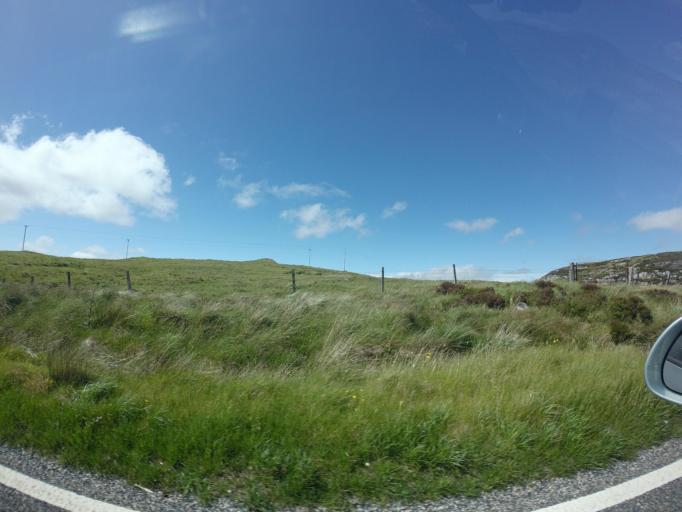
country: GB
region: Scotland
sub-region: Eilean Siar
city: Stornoway
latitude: 58.1155
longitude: -6.5124
